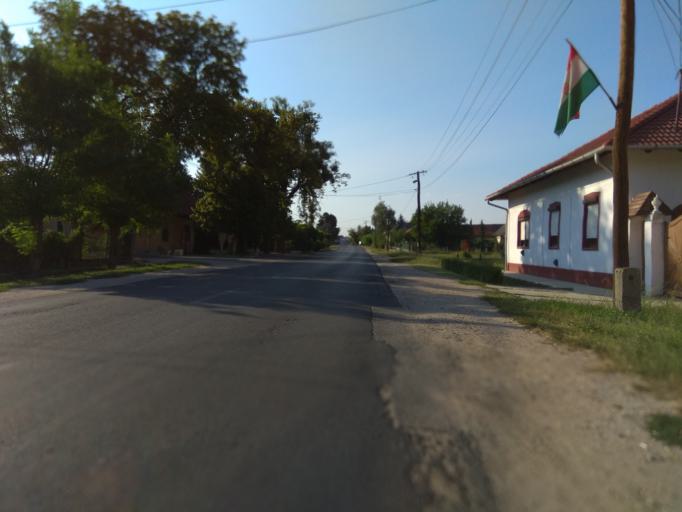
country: HU
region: Borsod-Abauj-Zemplen
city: Onod
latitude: 48.0050
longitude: 20.9161
